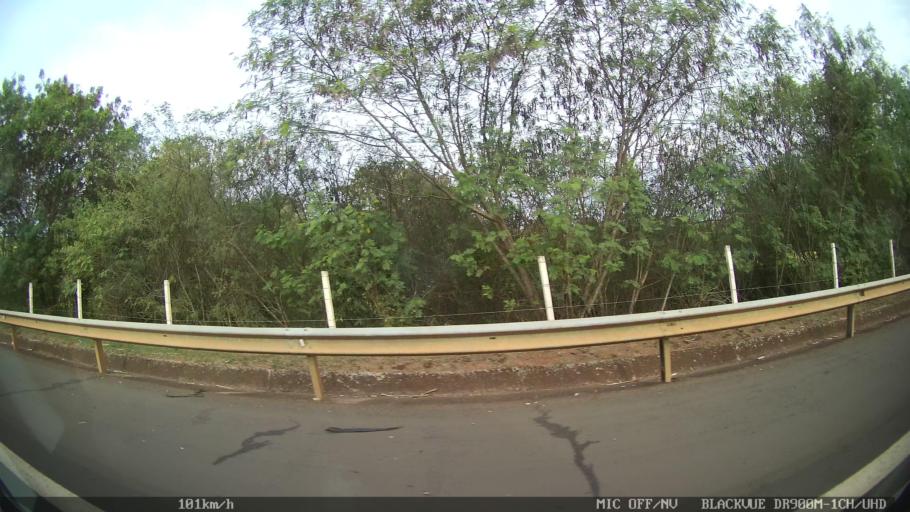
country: BR
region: Sao Paulo
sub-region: Iracemapolis
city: Iracemapolis
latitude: -22.6233
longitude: -47.4929
